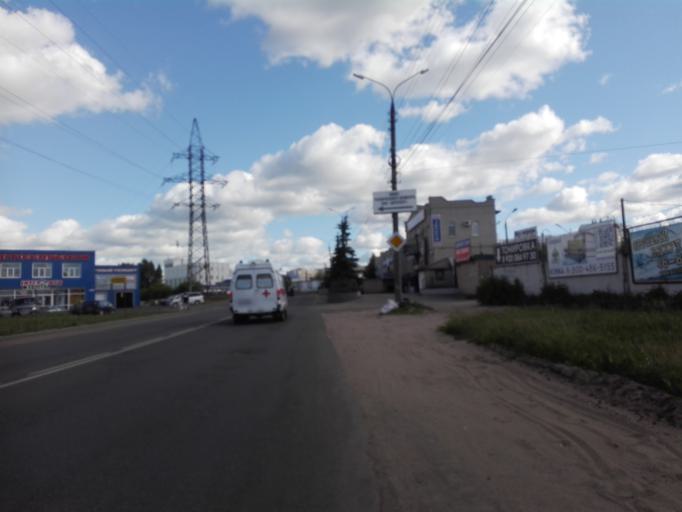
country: RU
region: Orjol
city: Orel
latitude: 52.9397
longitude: 36.0325
